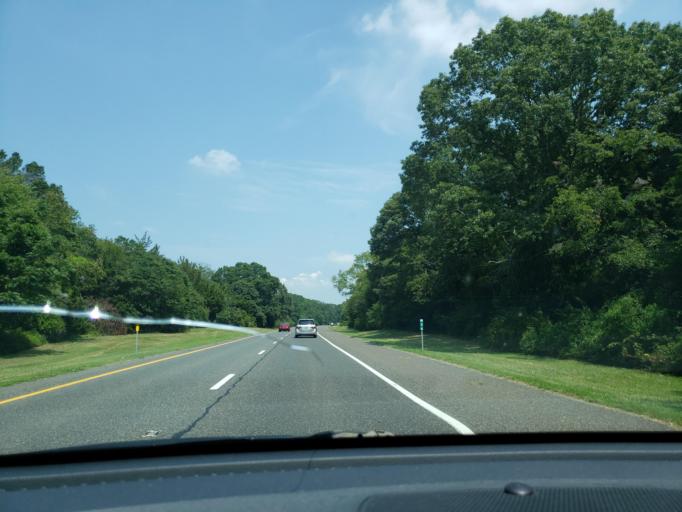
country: US
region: New Jersey
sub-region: Cape May County
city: Rio Grande
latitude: 38.9930
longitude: -74.8795
